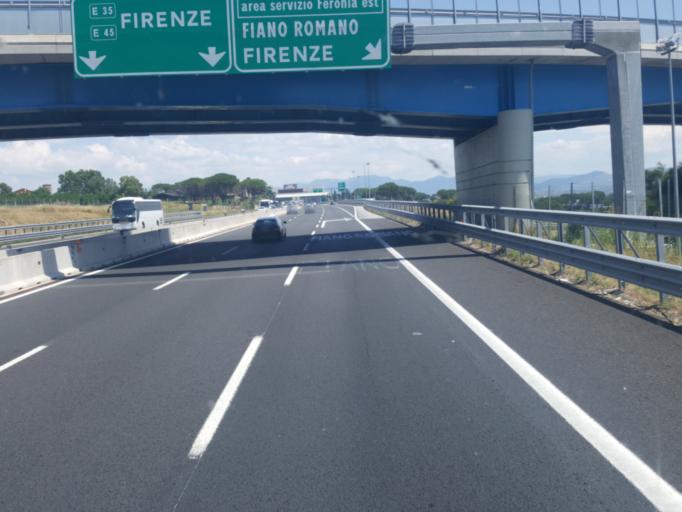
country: IT
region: Latium
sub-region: Citta metropolitana di Roma Capitale
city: Bivio di Capanelle
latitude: 42.1289
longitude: 12.5991
